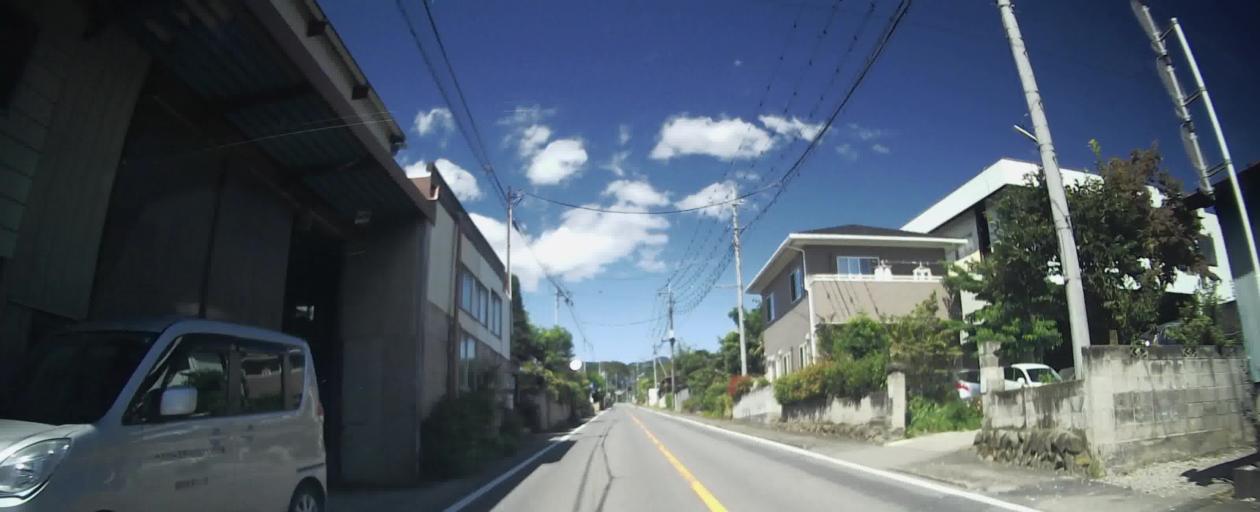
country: JP
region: Gunma
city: Kanekomachi
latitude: 36.4050
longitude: 138.9561
